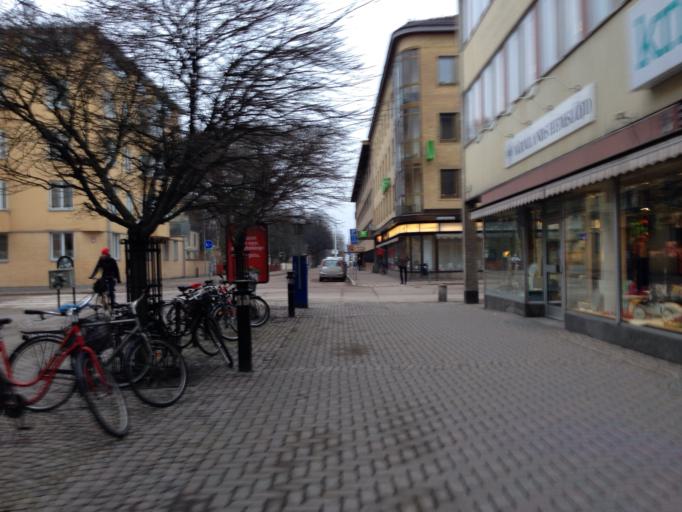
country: SE
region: Vaermland
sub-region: Karlstads Kommun
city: Karlstad
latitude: 59.3818
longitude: 13.5020
